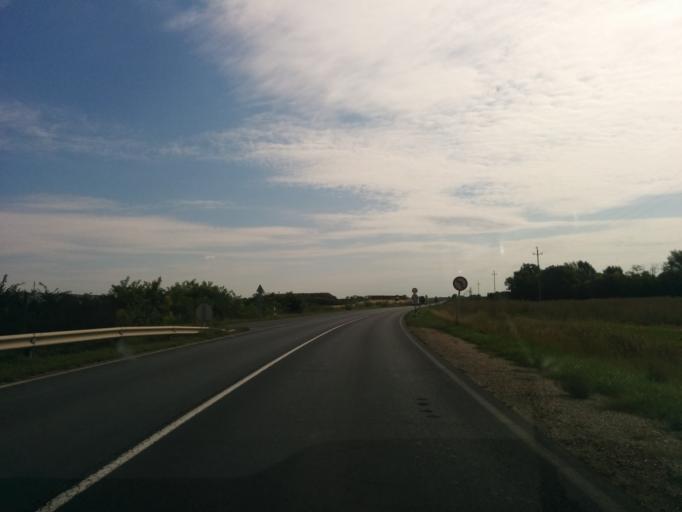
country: HU
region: Gyor-Moson-Sopron
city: Kony
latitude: 47.6381
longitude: 17.3434
